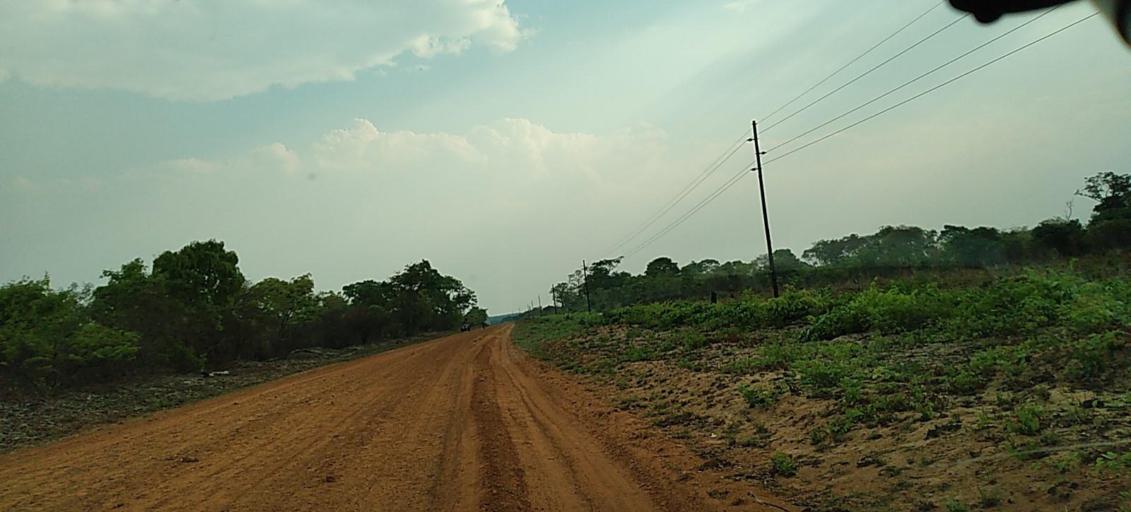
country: ZM
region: Western
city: Lukulu
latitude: -13.9020
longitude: 23.6552
